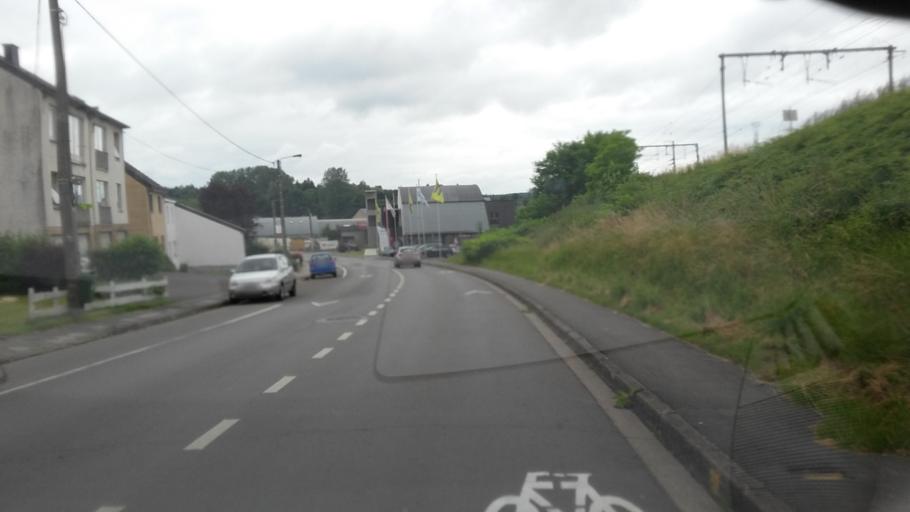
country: BE
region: Wallonia
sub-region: Province du Luxembourg
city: Arlon
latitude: 49.6836
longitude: 5.7989
